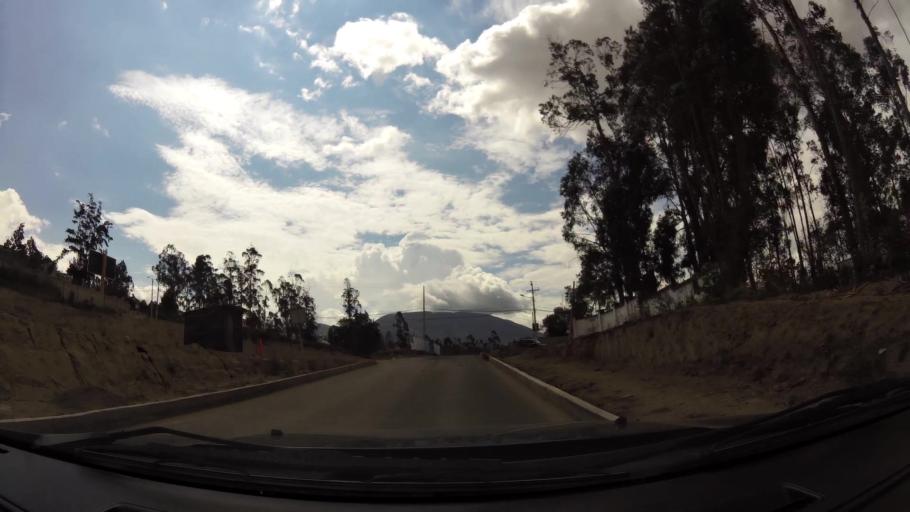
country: EC
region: Pichincha
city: Quito
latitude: -0.0984
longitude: -78.4607
